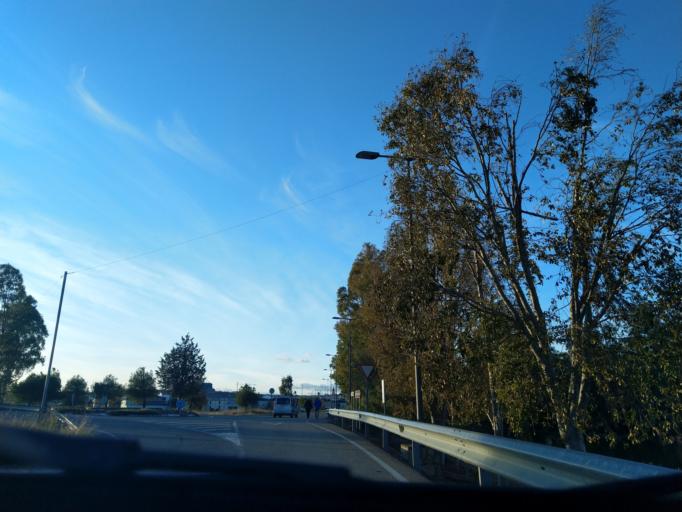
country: ES
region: Extremadura
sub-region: Provincia de Badajoz
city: Berlanga
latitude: 38.2754
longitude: -5.8197
